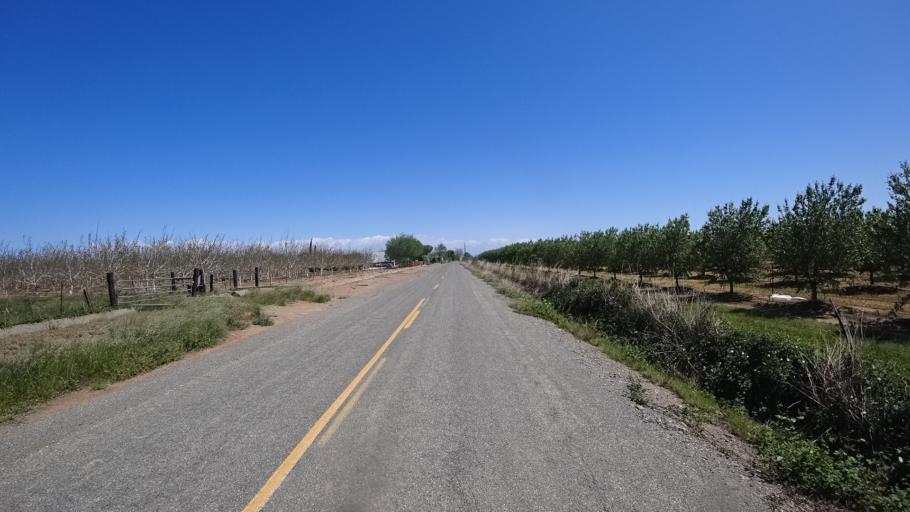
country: US
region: California
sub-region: Glenn County
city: Orland
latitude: 39.7948
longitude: -122.2142
